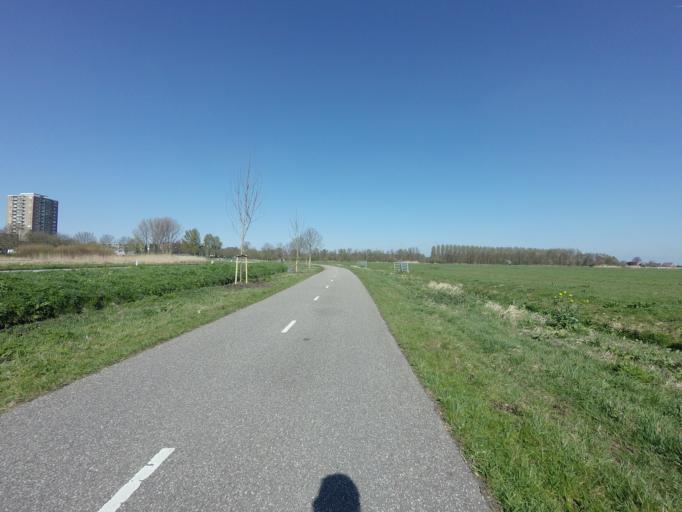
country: NL
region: North Holland
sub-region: Gemeente Haarlem
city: Haarlem
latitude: 52.3590
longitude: 4.6696
